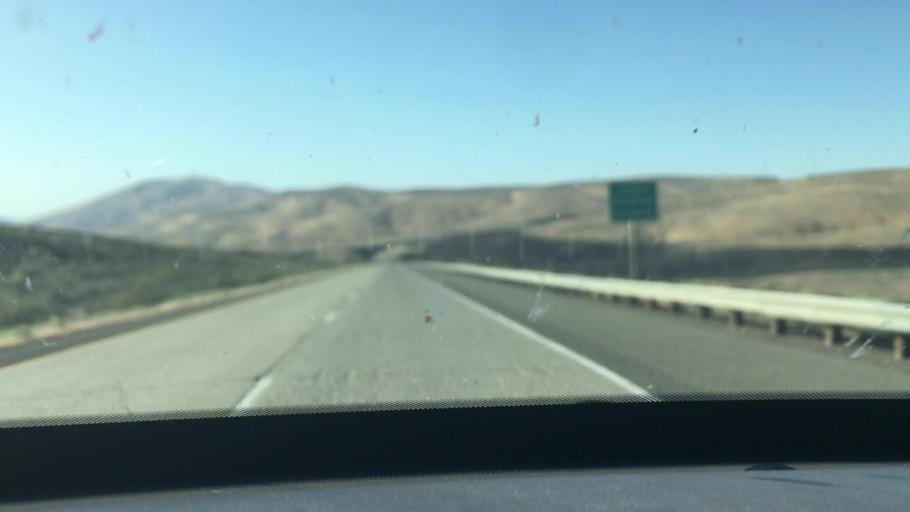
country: US
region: Washington
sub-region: Yakima County
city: Terrace Heights
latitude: 46.7370
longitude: -120.3855
